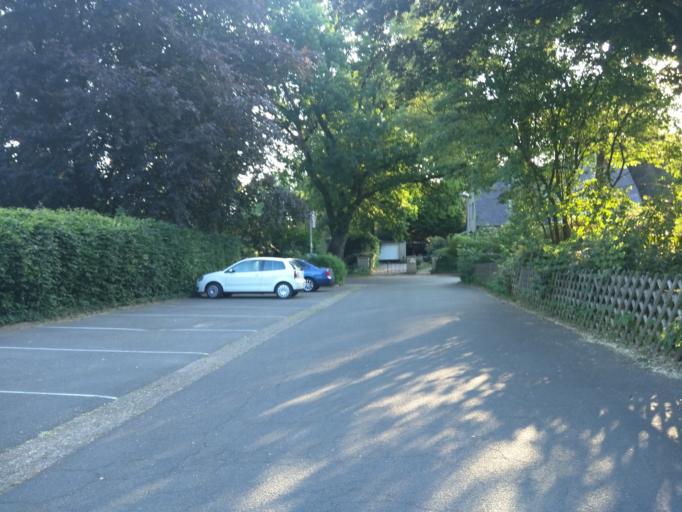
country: DE
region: Schleswig-Holstein
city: Grosshansdorf
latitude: 53.6495
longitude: 10.2786
